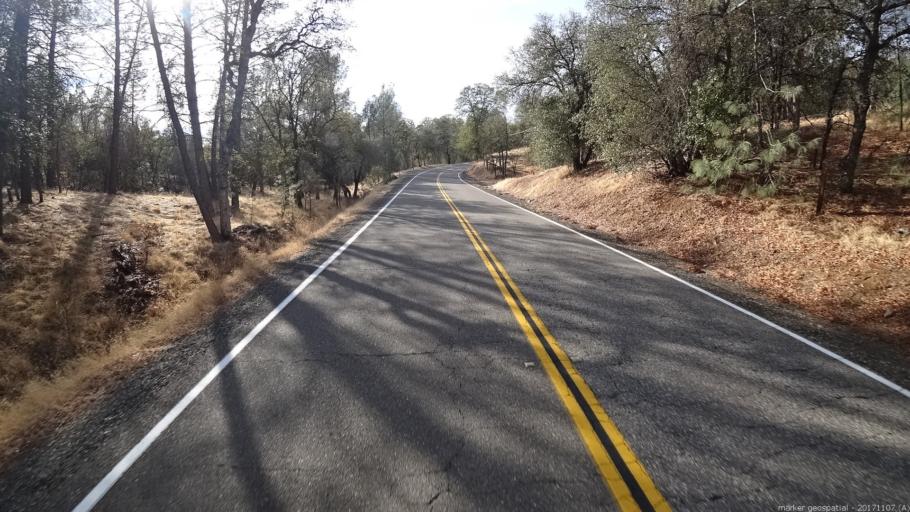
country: US
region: California
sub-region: Shasta County
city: Shasta
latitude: 40.5153
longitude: -122.5098
